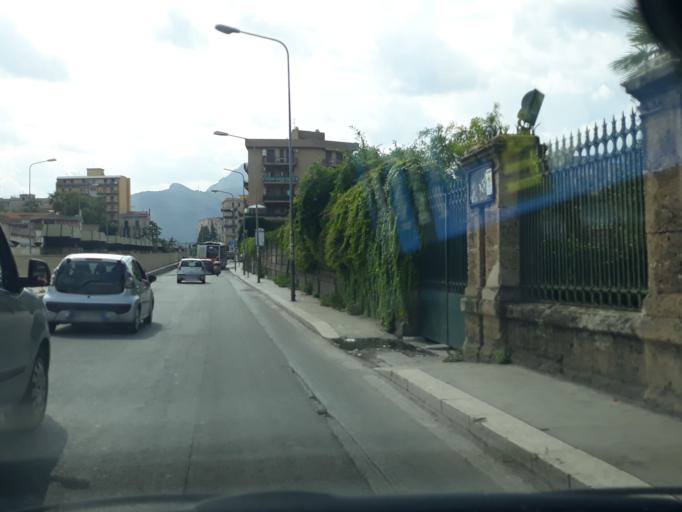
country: IT
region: Sicily
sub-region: Palermo
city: Palermo
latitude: 38.1095
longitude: 13.3534
